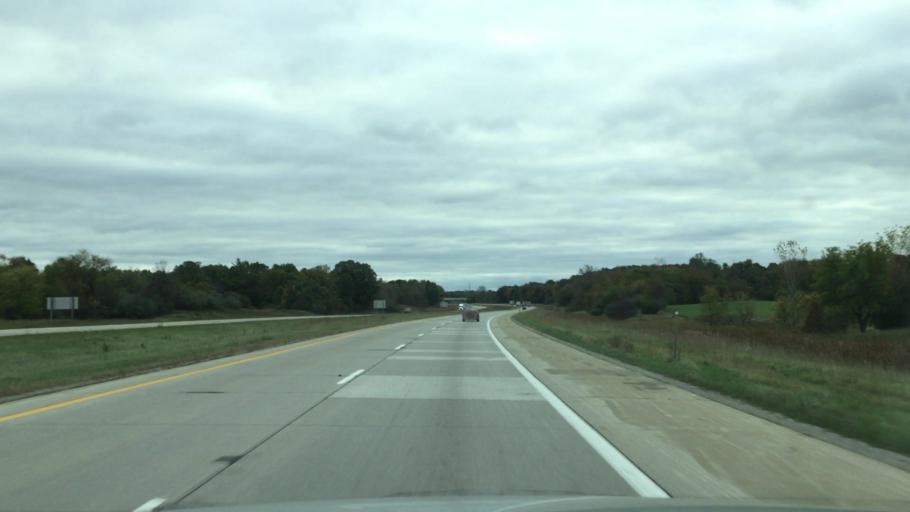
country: US
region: Michigan
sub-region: Lapeer County
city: Lapeer
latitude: 43.0200
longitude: -83.2954
